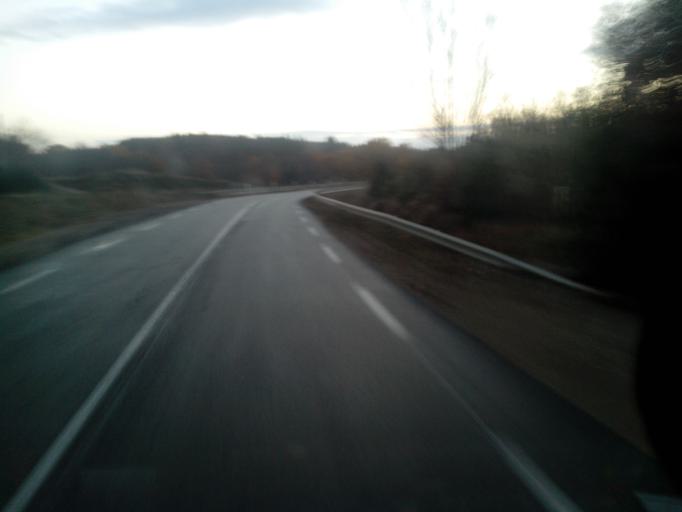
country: FR
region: Languedoc-Roussillon
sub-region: Departement de l'Herault
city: Gignac
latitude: 43.6649
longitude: 3.5662
